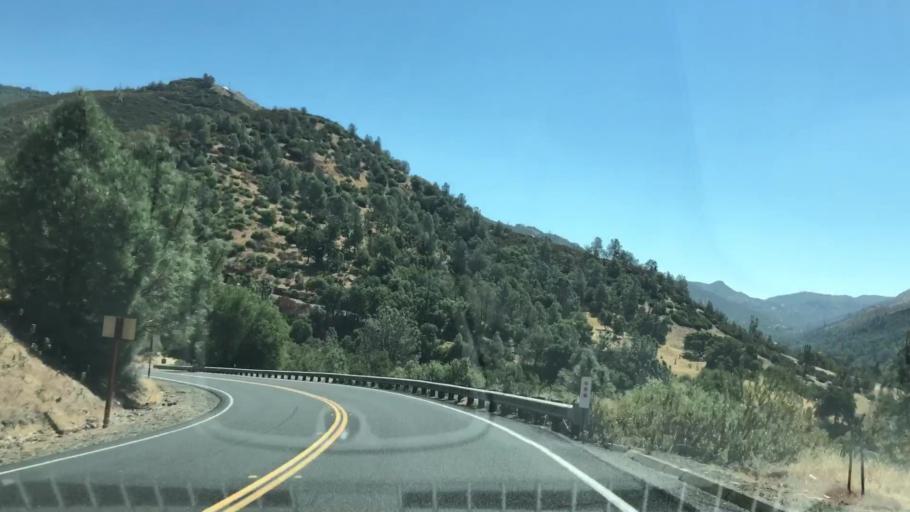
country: US
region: California
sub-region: Tuolumne County
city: Tuolumne City
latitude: 37.8171
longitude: -120.3003
